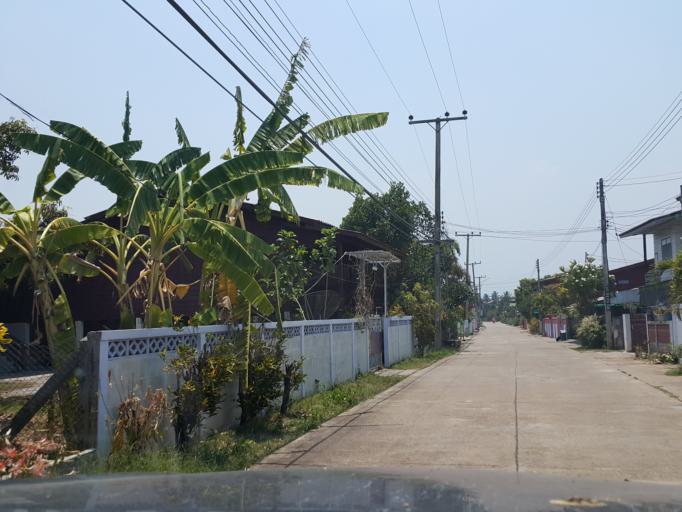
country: TH
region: Lampang
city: Thoen
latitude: 17.6387
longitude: 99.2601
